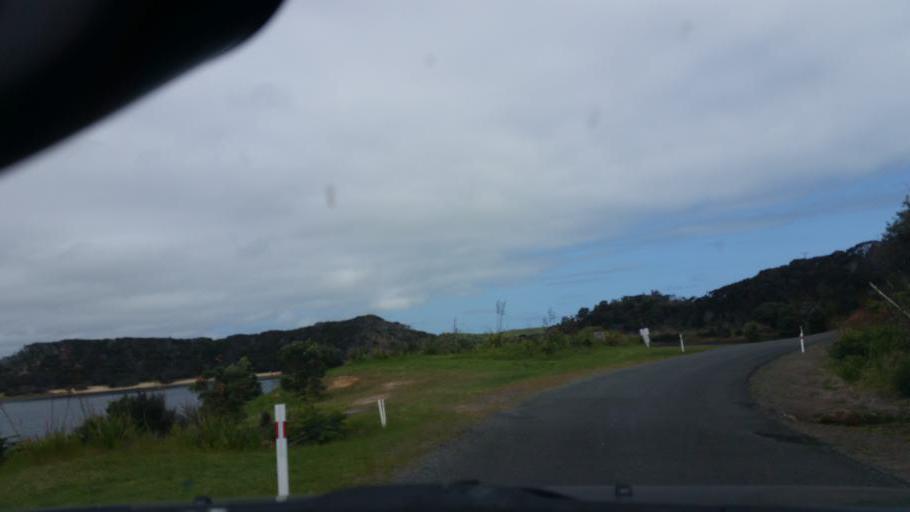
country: NZ
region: Northland
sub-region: Kaipara District
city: Dargaville
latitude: -35.7994
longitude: 173.6275
